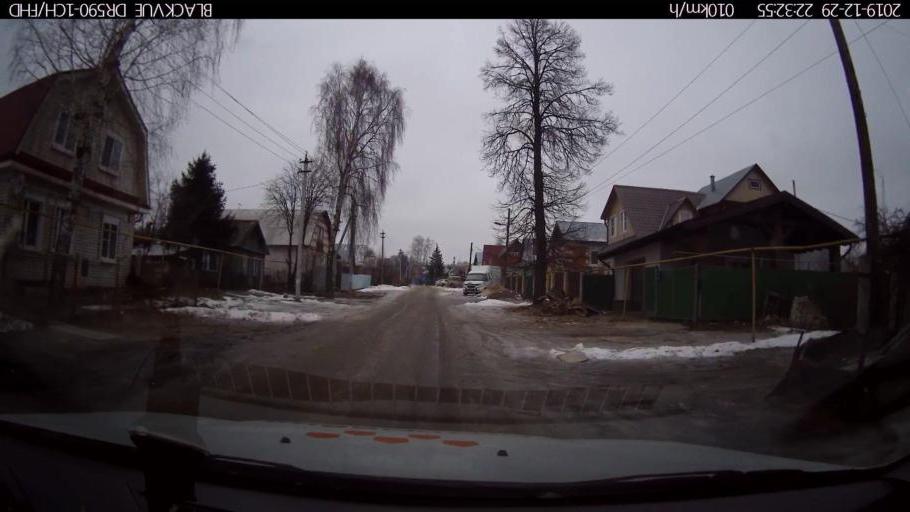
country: RU
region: Nizjnij Novgorod
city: Afonino
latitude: 56.2015
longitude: 43.9856
